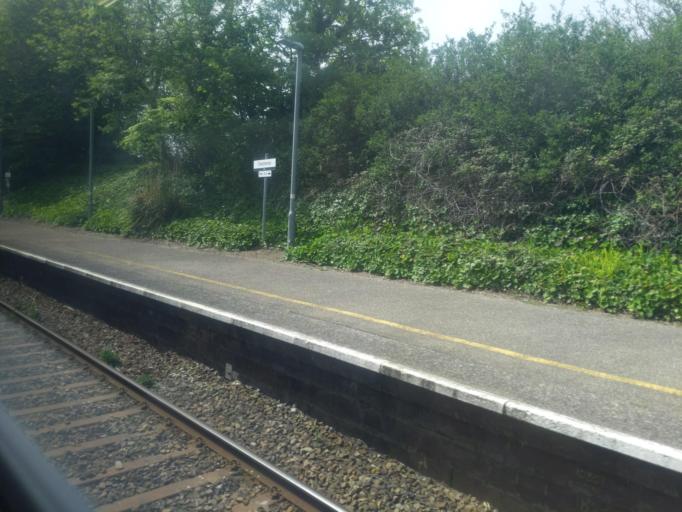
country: GB
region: England
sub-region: Cornwall
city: Camborne
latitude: 50.2099
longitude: -5.2985
